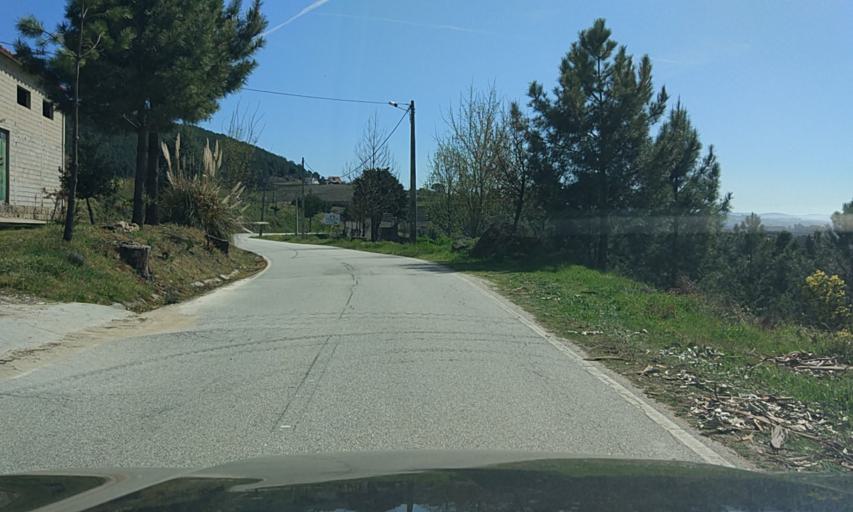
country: PT
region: Vila Real
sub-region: Sabrosa
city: Sabrosa
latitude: 41.3355
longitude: -7.5783
